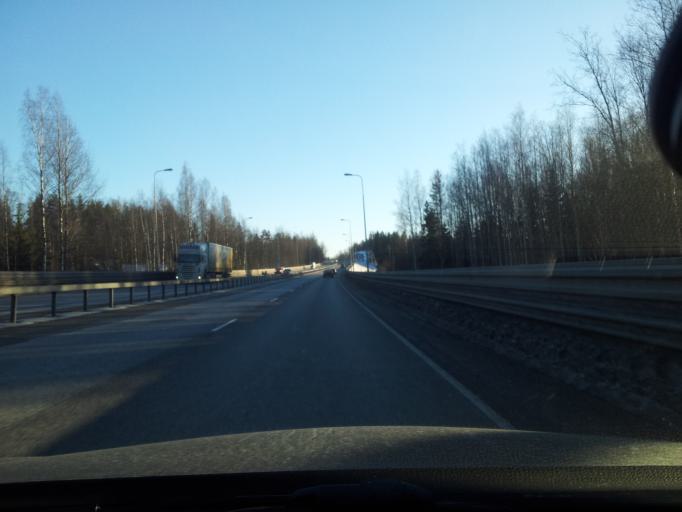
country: FI
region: Uusimaa
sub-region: Helsinki
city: Vihti
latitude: 60.3119
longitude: 24.3487
